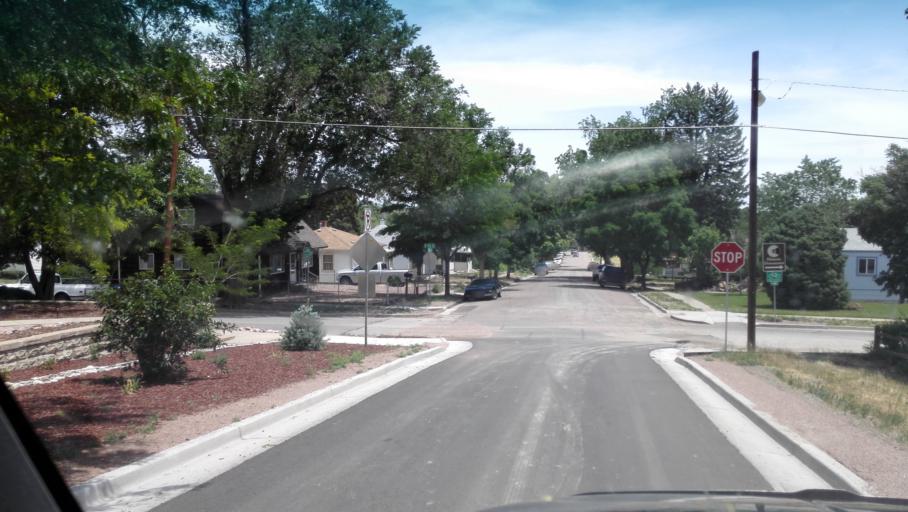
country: US
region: Colorado
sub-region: Fremont County
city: Canon City
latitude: 38.4485
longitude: -105.2453
